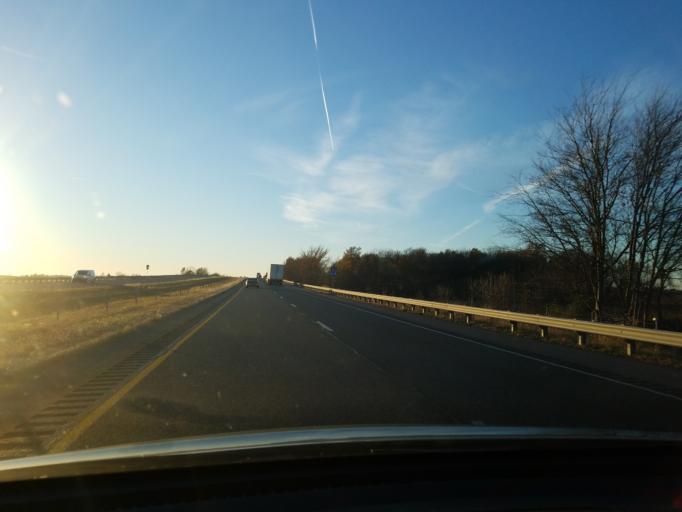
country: US
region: Indiana
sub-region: Gibson County
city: Haubstadt
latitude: 38.1671
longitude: -87.5594
